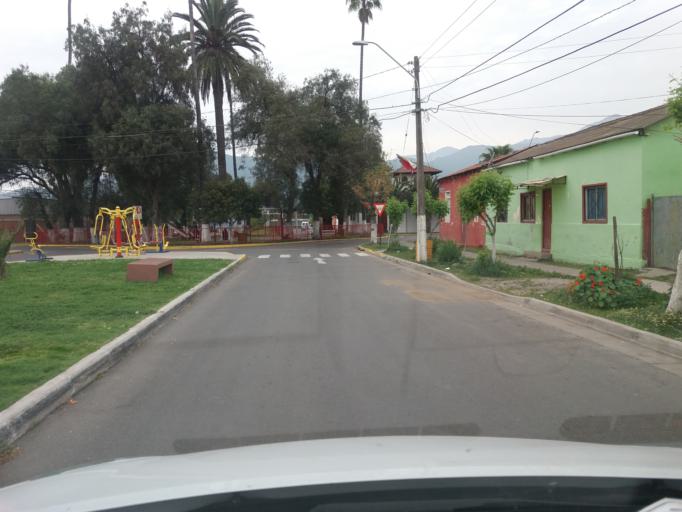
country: CL
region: Valparaiso
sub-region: Provincia de Quillota
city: Hacienda La Calera
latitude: -32.7784
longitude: -71.1846
